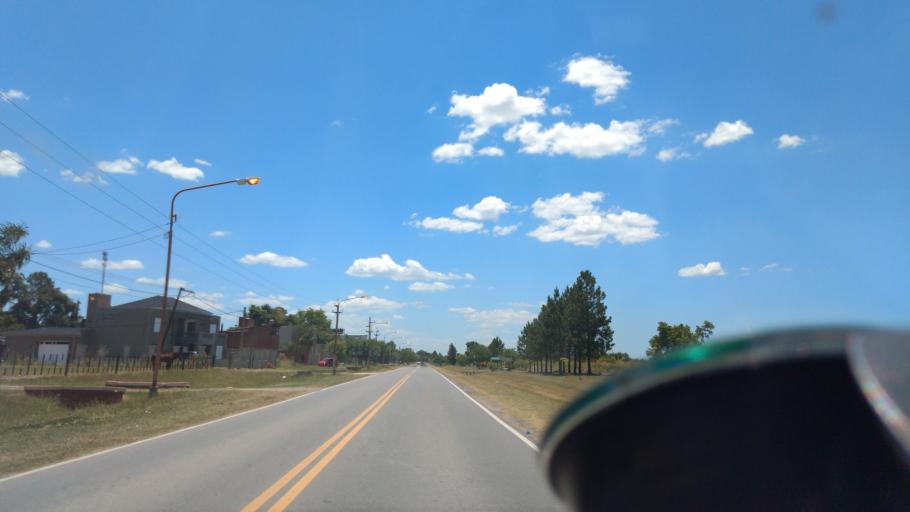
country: AR
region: Santa Fe
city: Laguna Paiva
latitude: -31.3224
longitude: -60.6589
